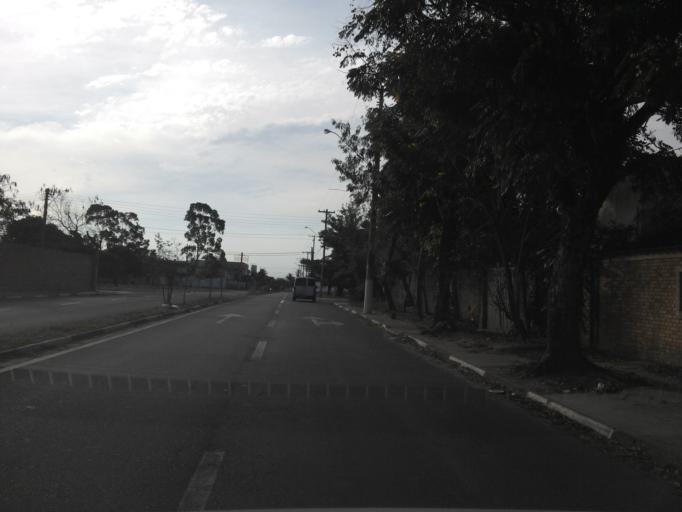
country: BR
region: Sao Paulo
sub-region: Hortolandia
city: Hortolandia
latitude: -22.9099
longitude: -47.2090
